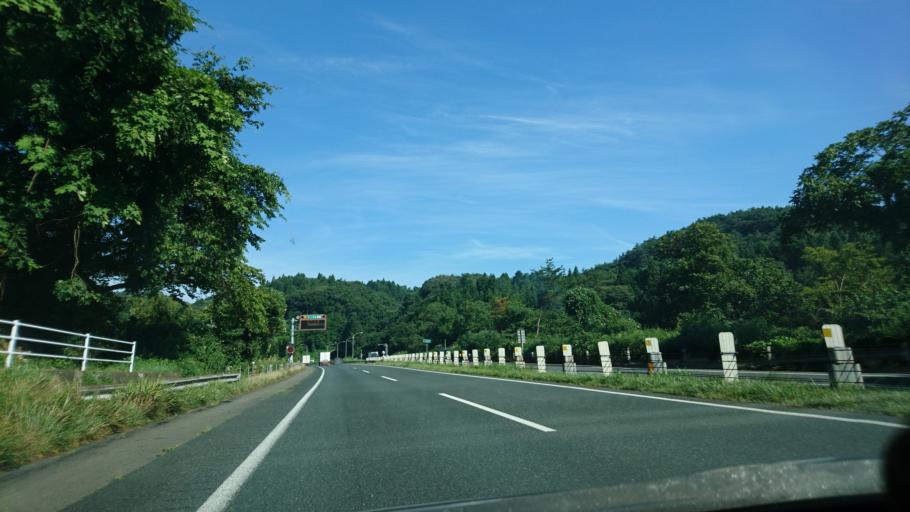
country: JP
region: Iwate
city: Ichinoseki
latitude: 38.9868
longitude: 141.1044
